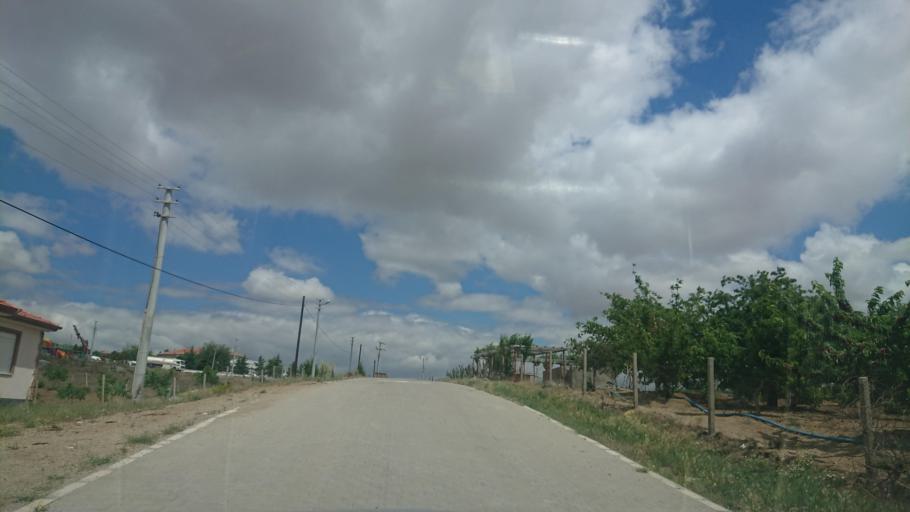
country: TR
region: Aksaray
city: Agacoren
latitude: 38.8682
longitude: 33.9467
